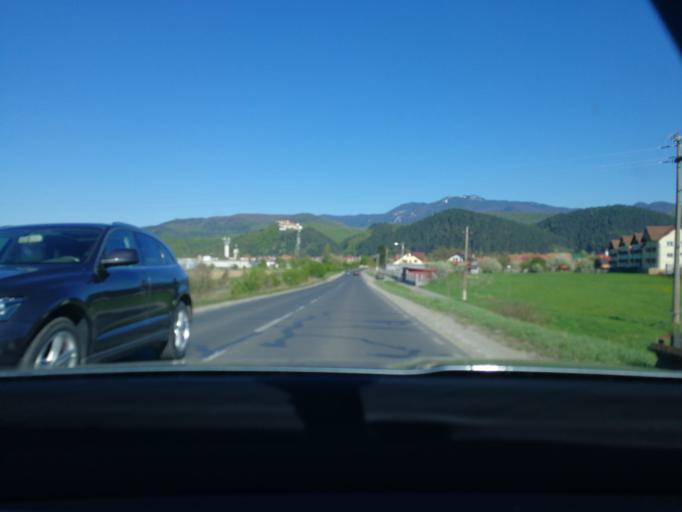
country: RO
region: Brasov
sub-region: Oras Rasnov
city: Rasnov
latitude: 45.5898
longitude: 25.4468
